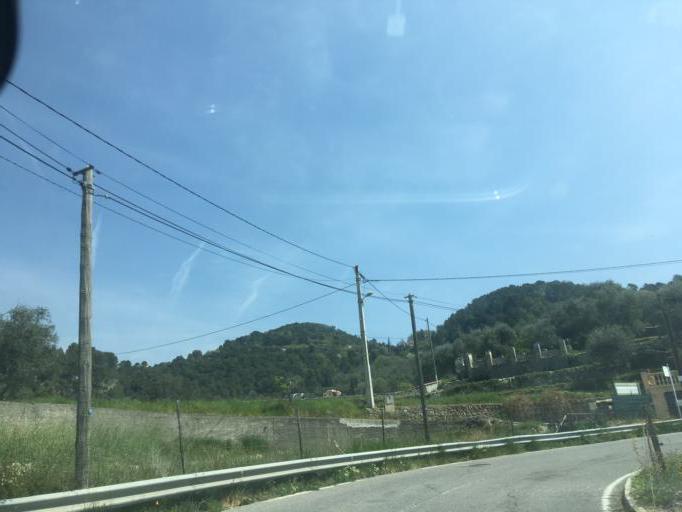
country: FR
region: Provence-Alpes-Cote d'Azur
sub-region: Departement des Alpes-Maritimes
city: Saint-Martin-du-Var
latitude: 43.8315
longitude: 7.1982
